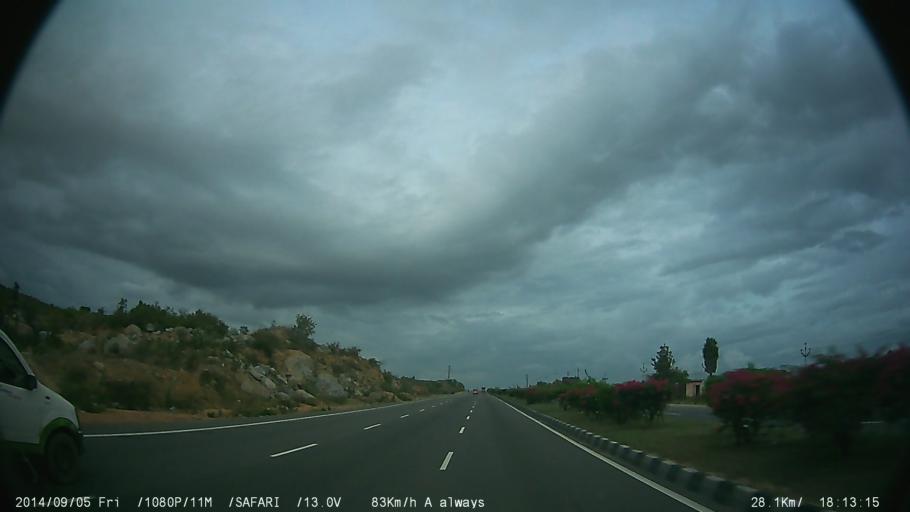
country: IN
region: Tamil Nadu
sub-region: Krishnagiri
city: Hosur
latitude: 12.6871
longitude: 77.9276
